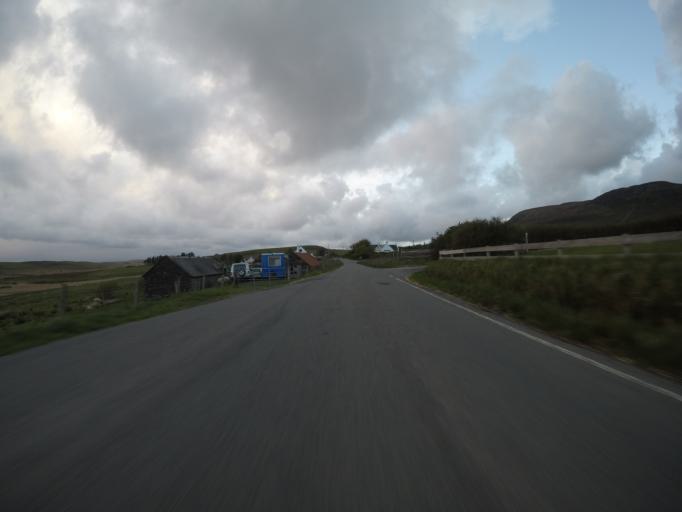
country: GB
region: Scotland
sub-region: Highland
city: Portree
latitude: 57.6171
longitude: -6.3720
